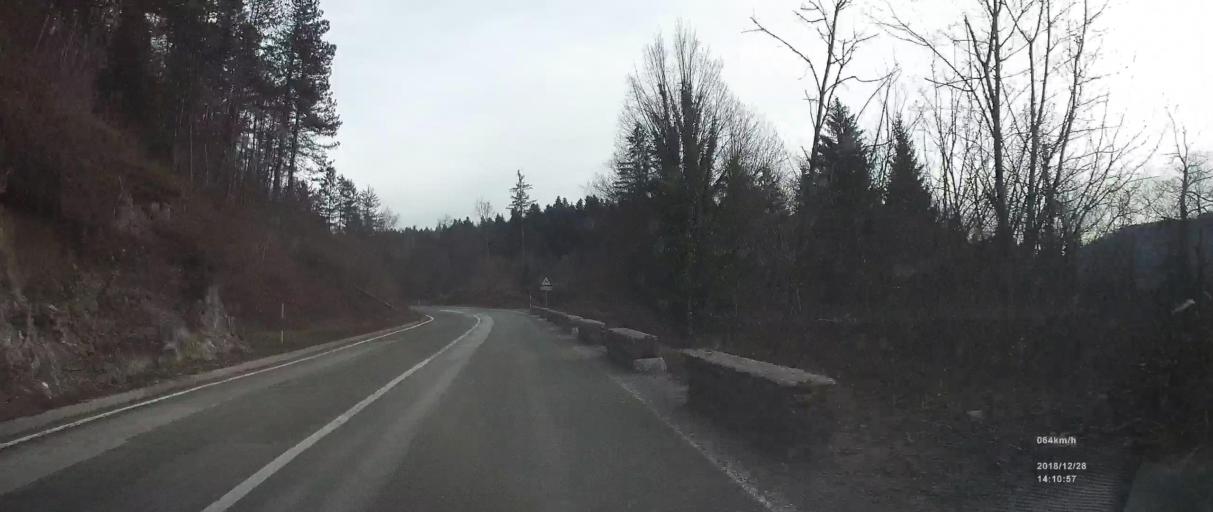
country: SI
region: Kostel
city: Kostel
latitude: 45.4500
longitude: 14.9798
